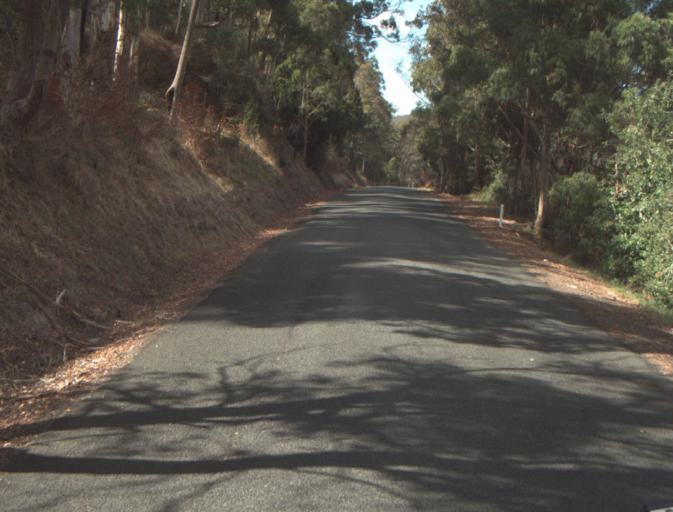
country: AU
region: Tasmania
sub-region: Launceston
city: Mayfield
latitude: -41.2435
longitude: 147.1504
